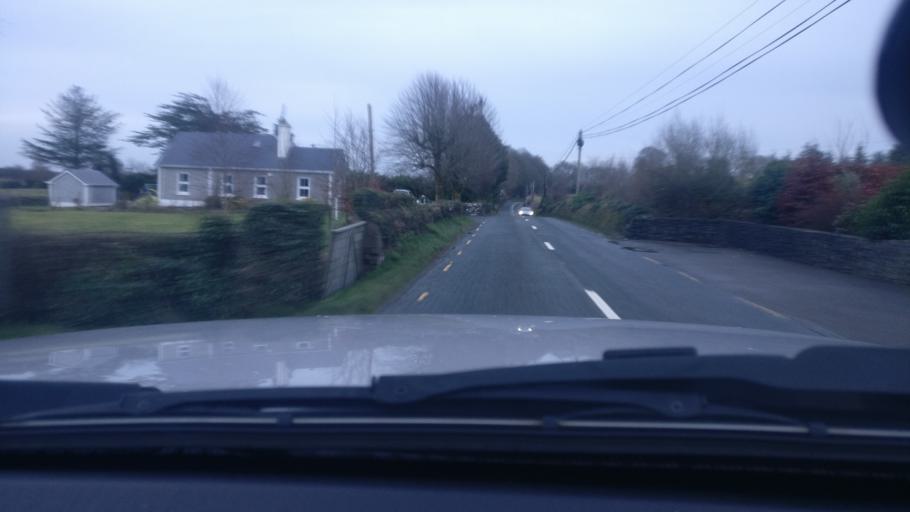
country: IE
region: Connaught
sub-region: County Galway
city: Loughrea
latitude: 53.1734
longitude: -8.5289
